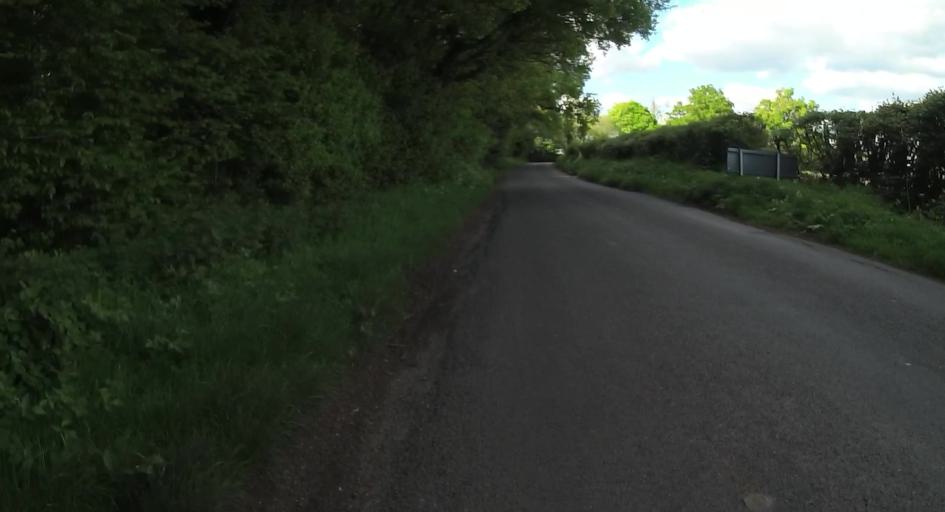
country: GB
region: England
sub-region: West Berkshire
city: Stratfield Mortimer
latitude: 51.3570
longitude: -1.0435
